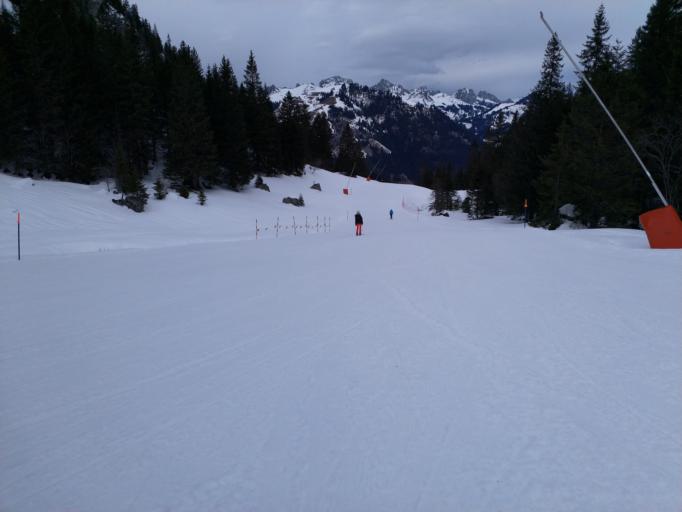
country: CH
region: Bern
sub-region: Obersimmental-Saanen District
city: Saanen
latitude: 46.4643
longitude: 7.2236
